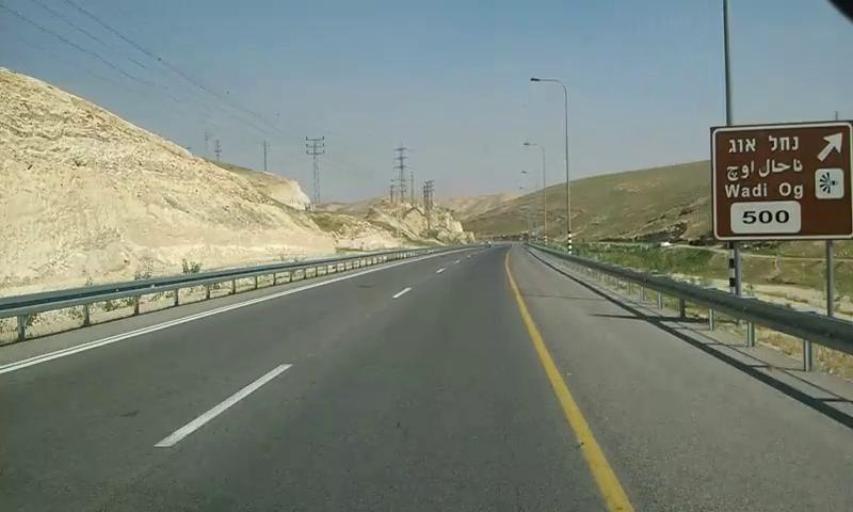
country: PS
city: Az Za`ayyim
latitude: 31.8088
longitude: 35.3349
